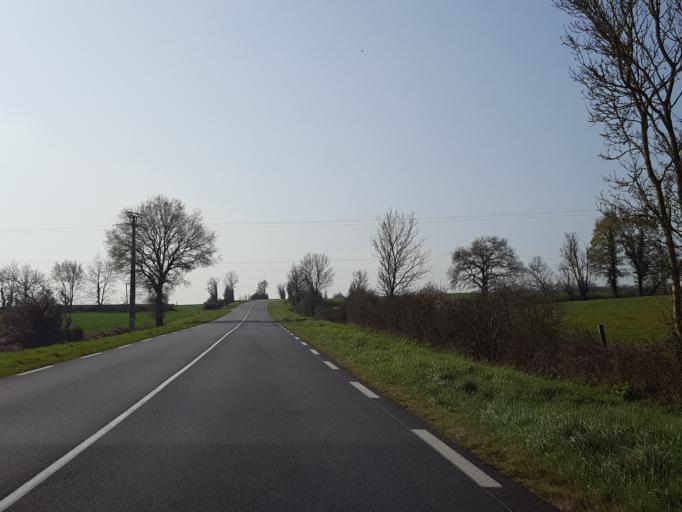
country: FR
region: Pays de la Loire
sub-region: Departement de la Vendee
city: Rocheserviere
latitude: 46.9118
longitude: -1.5050
